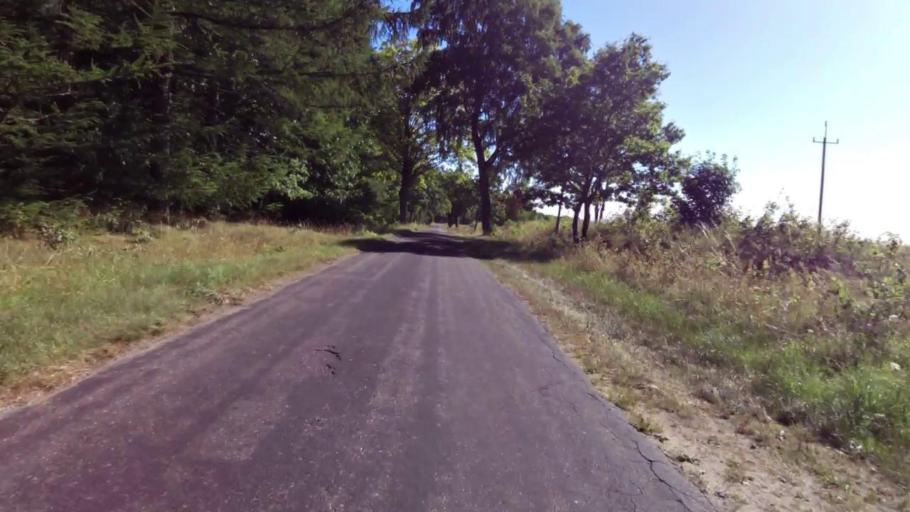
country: PL
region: West Pomeranian Voivodeship
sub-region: Powiat szczecinecki
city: Szczecinek
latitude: 53.7858
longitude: 16.6775
